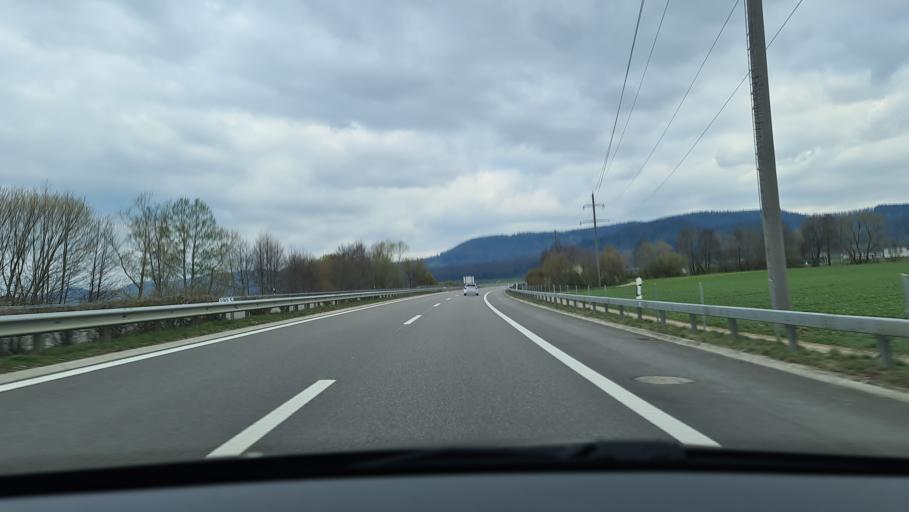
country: CH
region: Jura
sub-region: Porrentruy District
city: Alle
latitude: 47.4160
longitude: 7.1284
